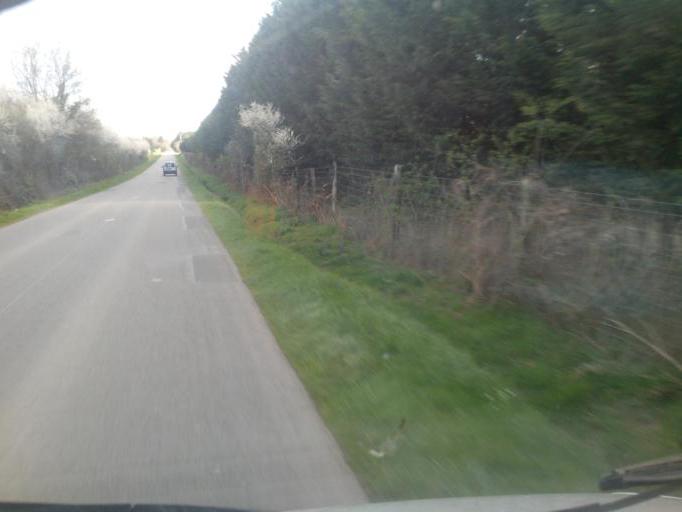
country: FR
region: Brittany
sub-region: Departement d'Ille-et-Vilaine
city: Grand-Fougeray
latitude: 47.7560
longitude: -1.7488
